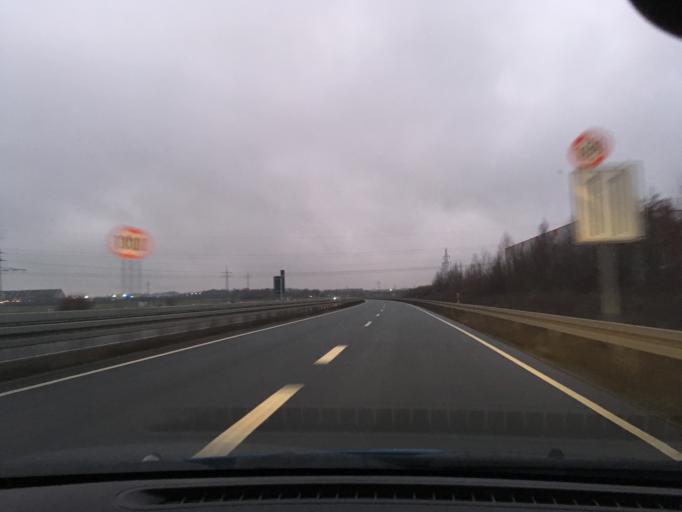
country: DE
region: Lower Saxony
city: Lehrte
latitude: 52.3575
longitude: 9.9064
